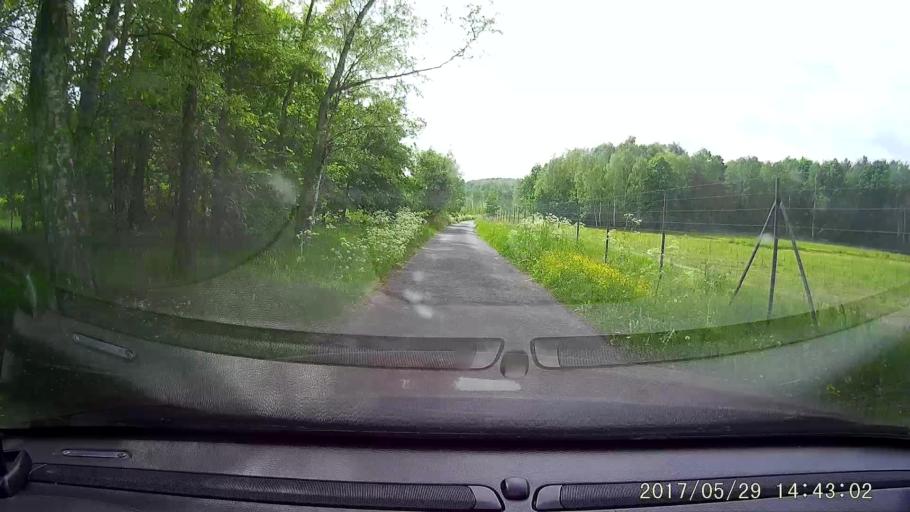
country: PL
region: Lower Silesian Voivodeship
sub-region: Powiat zgorzelecki
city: Wegliniec
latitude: 51.2380
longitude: 15.1950
